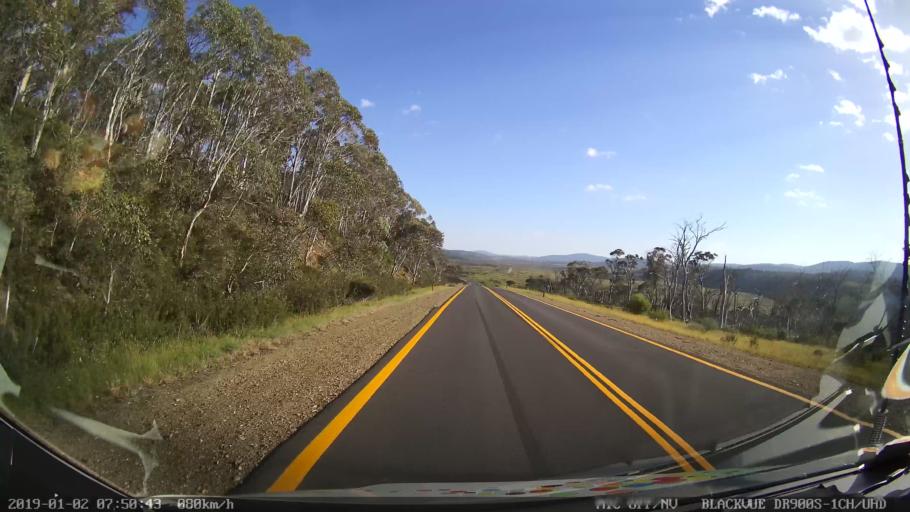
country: AU
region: New South Wales
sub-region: Tumut Shire
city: Tumut
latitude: -35.7270
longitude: 148.5287
